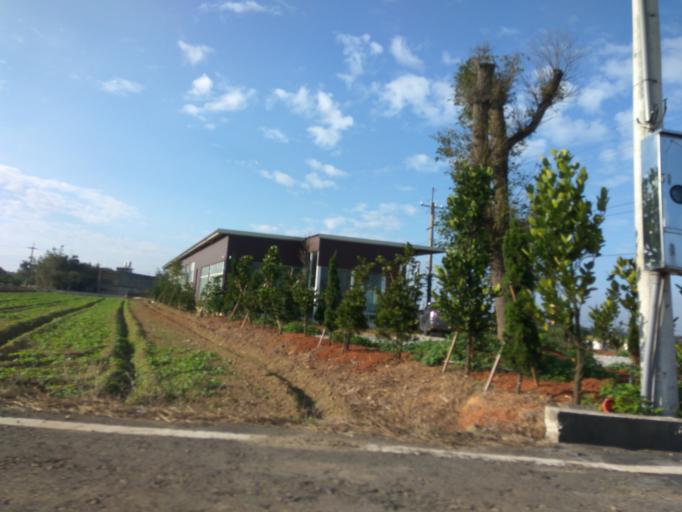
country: TW
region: Taiwan
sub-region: Hsinchu
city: Zhubei
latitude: 24.9781
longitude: 121.0575
